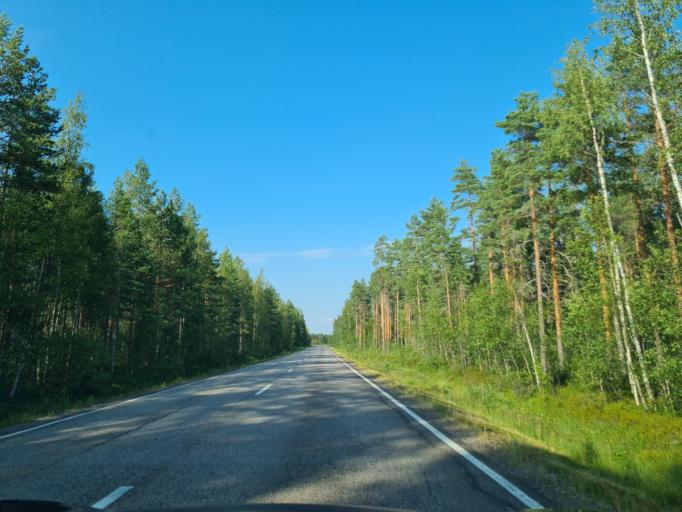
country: FI
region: Satakunta
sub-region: Pohjois-Satakunta
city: Karvia
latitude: 62.3087
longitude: 22.6490
